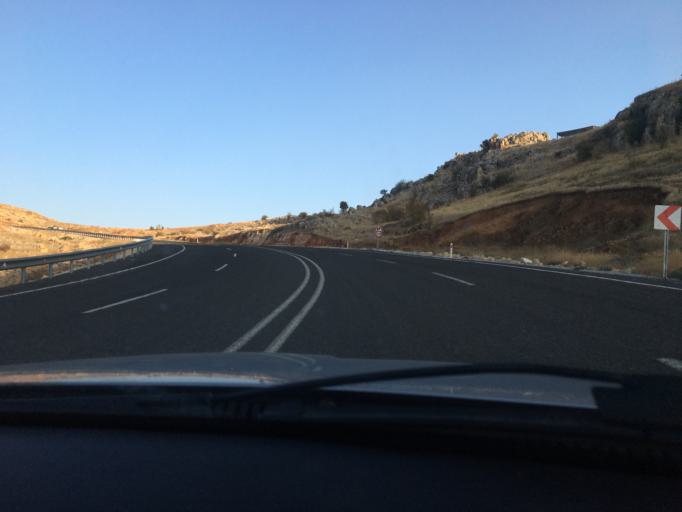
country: TR
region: Sanliurfa
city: Halfeti
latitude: 37.2386
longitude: 37.8778
